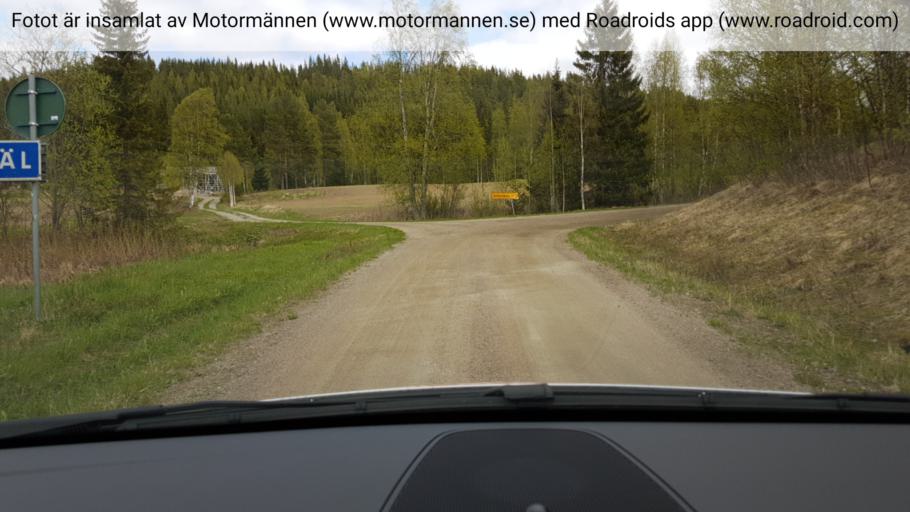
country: SE
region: Jaemtland
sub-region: Braecke Kommun
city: Braecke
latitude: 62.8016
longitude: 15.1241
